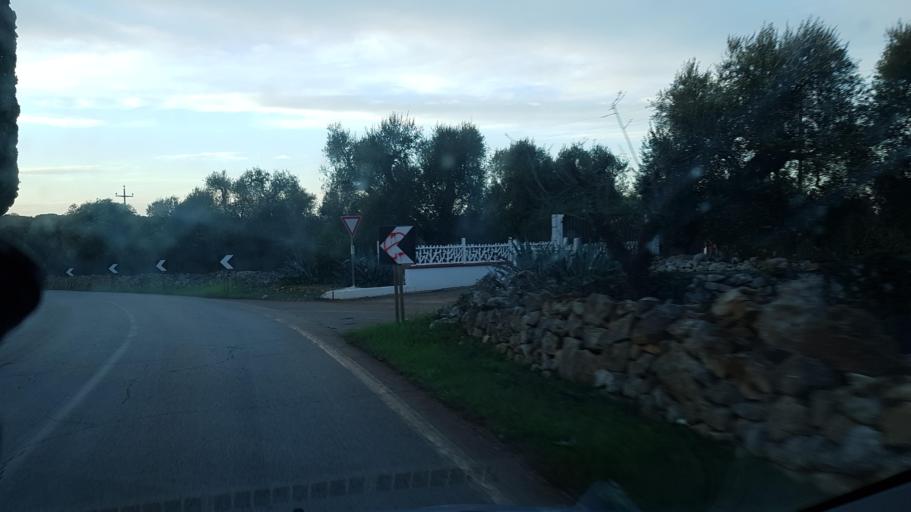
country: IT
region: Apulia
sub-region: Provincia di Brindisi
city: Ceglie Messapica
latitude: 40.6448
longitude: 17.5540
